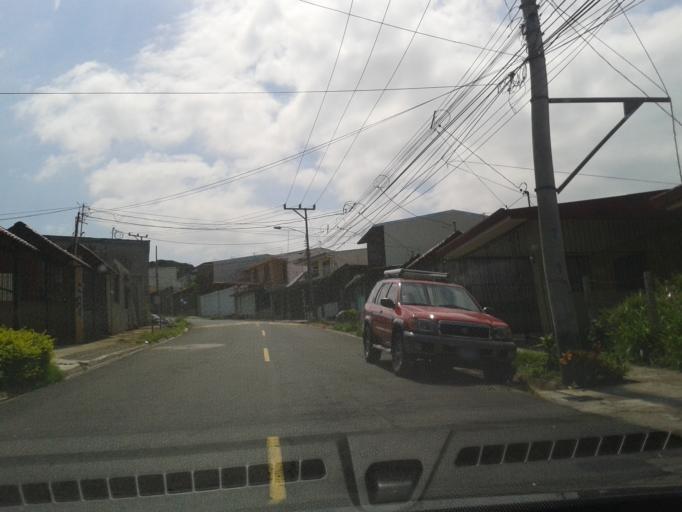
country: CR
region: Heredia
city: San Francisco
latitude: 9.9827
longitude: -84.1376
